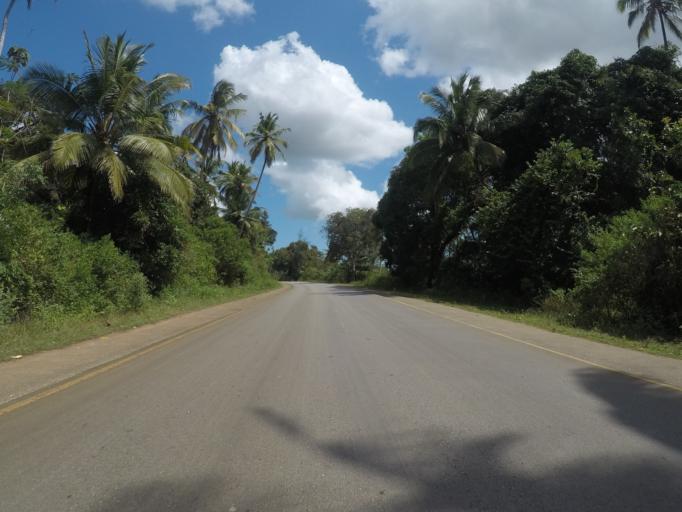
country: TZ
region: Zanzibar Central/South
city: Koani
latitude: -6.1721
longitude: 39.3297
